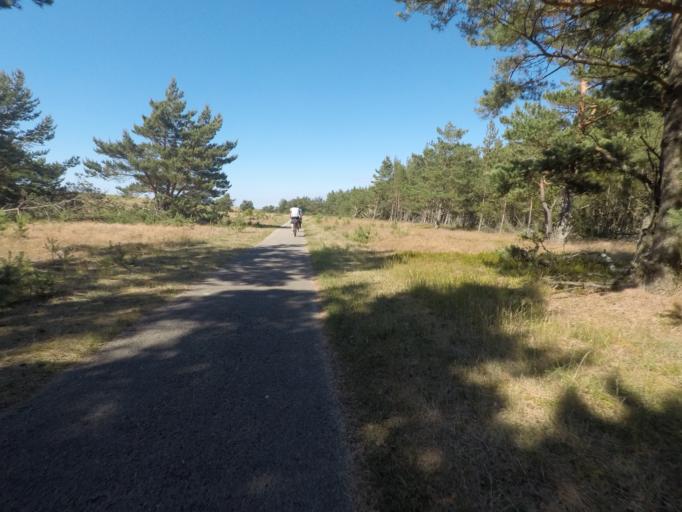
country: LT
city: Neringa
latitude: 55.4980
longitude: 21.0886
